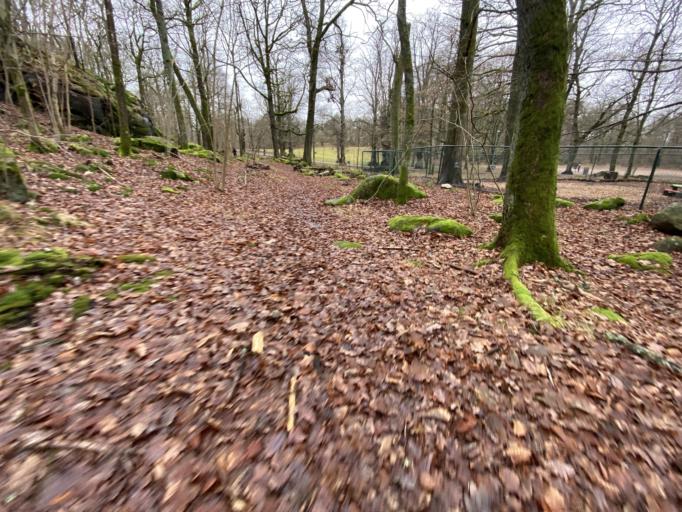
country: SE
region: Vaestra Goetaland
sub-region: Goteborg
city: Eriksbo
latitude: 57.7189
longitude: 12.0472
